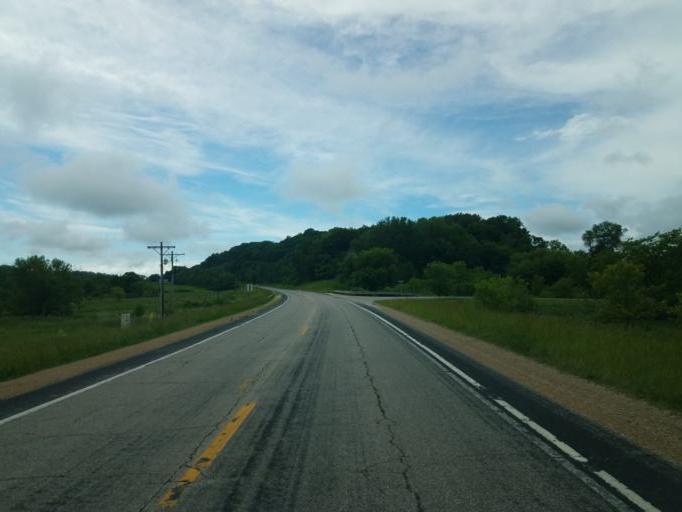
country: US
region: Wisconsin
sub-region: Vernon County
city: Hillsboro
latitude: 43.6599
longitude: -90.4015
